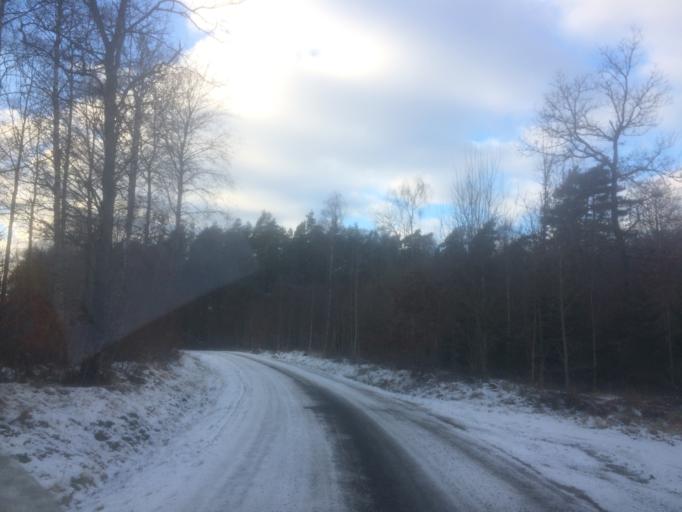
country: SE
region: Vaestra Goetaland
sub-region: Kungalvs Kommun
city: Kungalv
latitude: 57.8301
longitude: 11.9692
